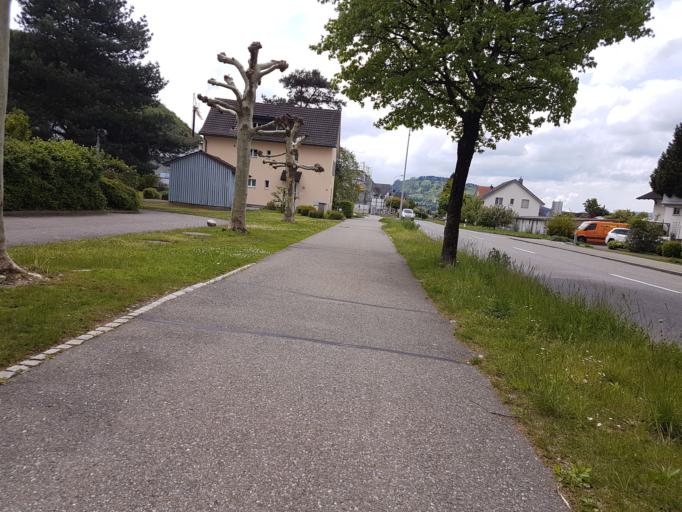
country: CH
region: Aargau
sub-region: Bezirk Baden
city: Wurenlingen
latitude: 47.5231
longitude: 8.2457
